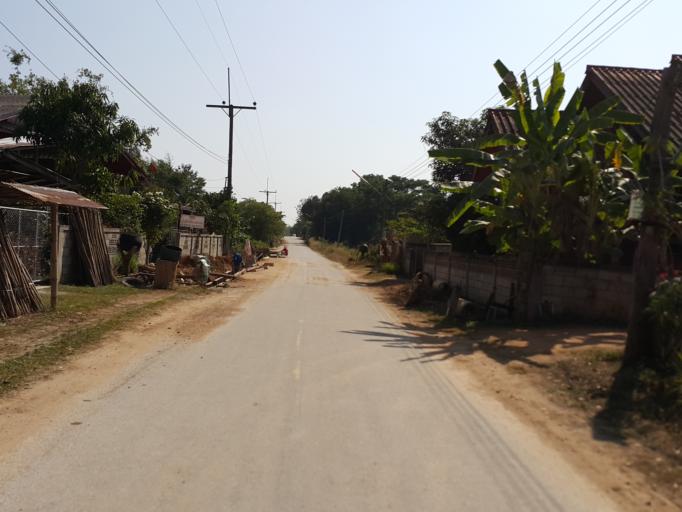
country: TH
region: Lampang
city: Wang Nuea
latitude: 19.0335
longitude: 99.6232
